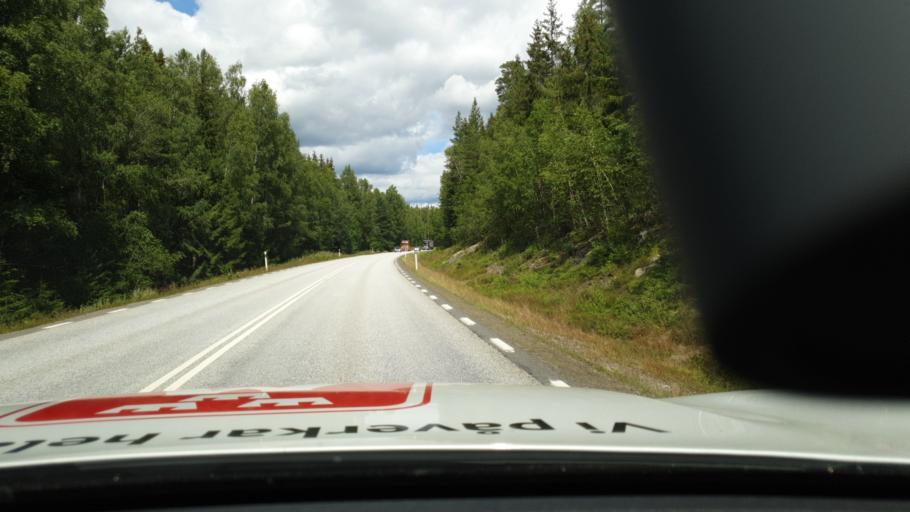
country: SE
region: Vaermland
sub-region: Storfors Kommun
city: Storfors
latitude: 59.4750
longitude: 14.3277
